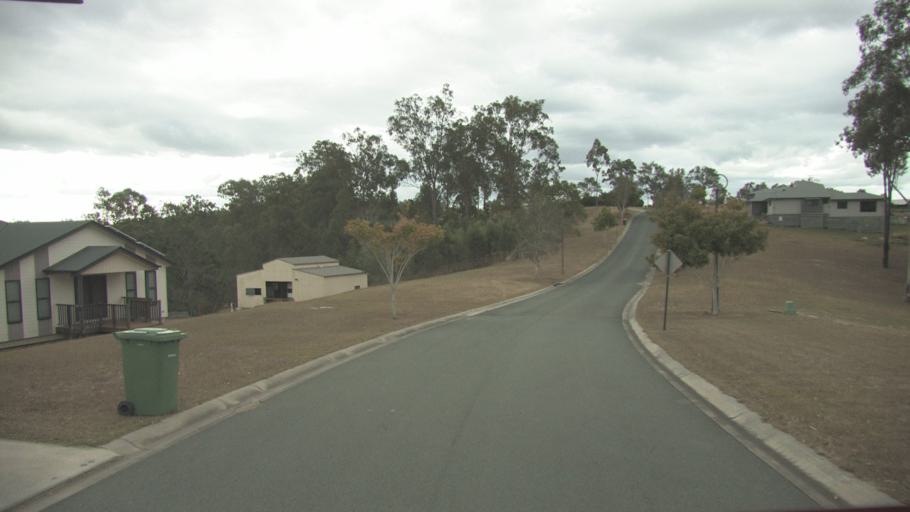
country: AU
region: Queensland
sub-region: Logan
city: Cedar Vale
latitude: -27.8704
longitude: 153.0716
